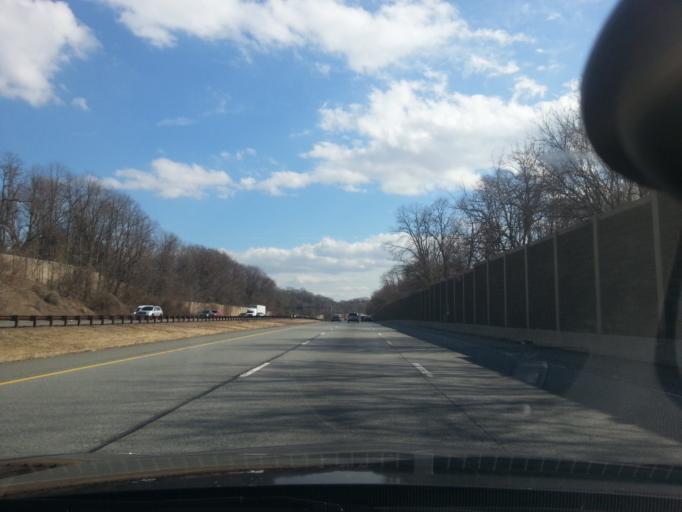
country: US
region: Pennsylvania
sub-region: Delaware County
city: Radnor
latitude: 40.0232
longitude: -75.3619
